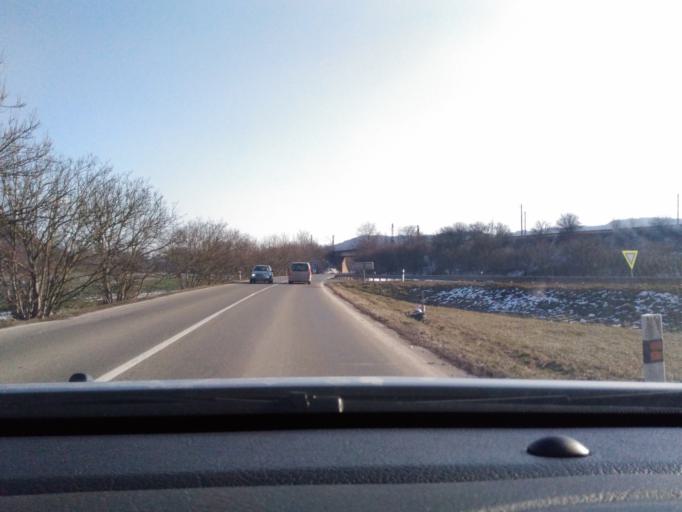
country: CZ
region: South Moravian
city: Predklasteri
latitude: 49.3607
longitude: 16.3985
